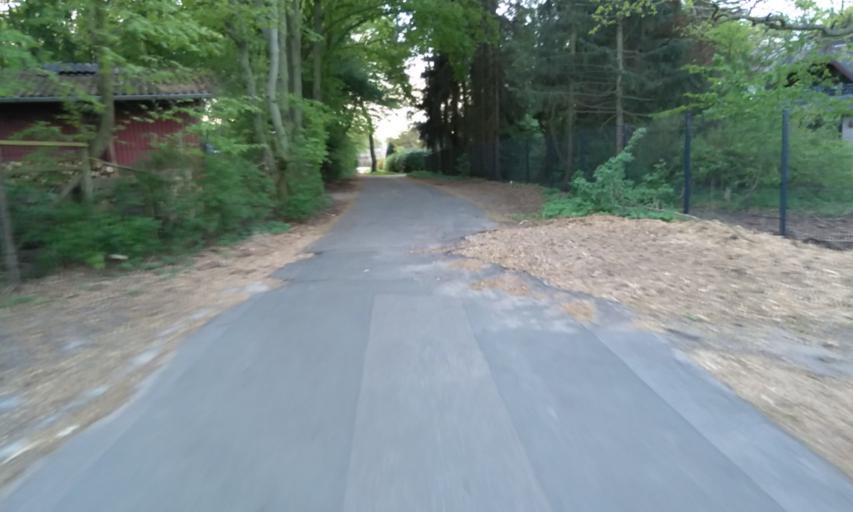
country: DE
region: Lower Saxony
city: Neuenkirchen
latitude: 53.5023
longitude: 9.5925
